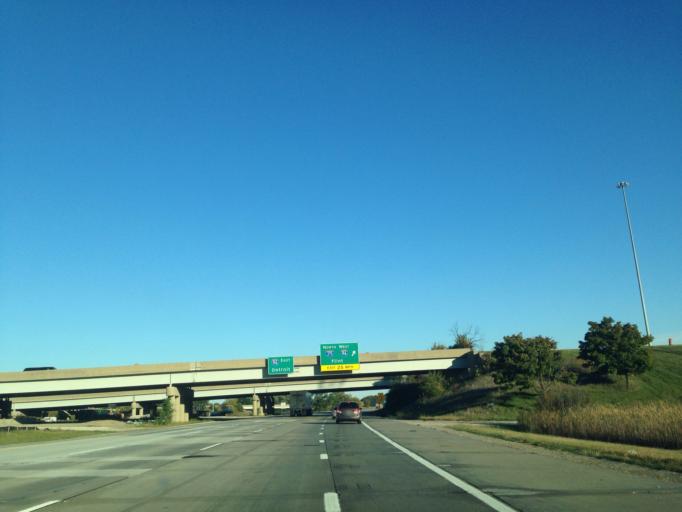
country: US
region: Michigan
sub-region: Wayne County
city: Plymouth
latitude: 42.3865
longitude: -83.4386
